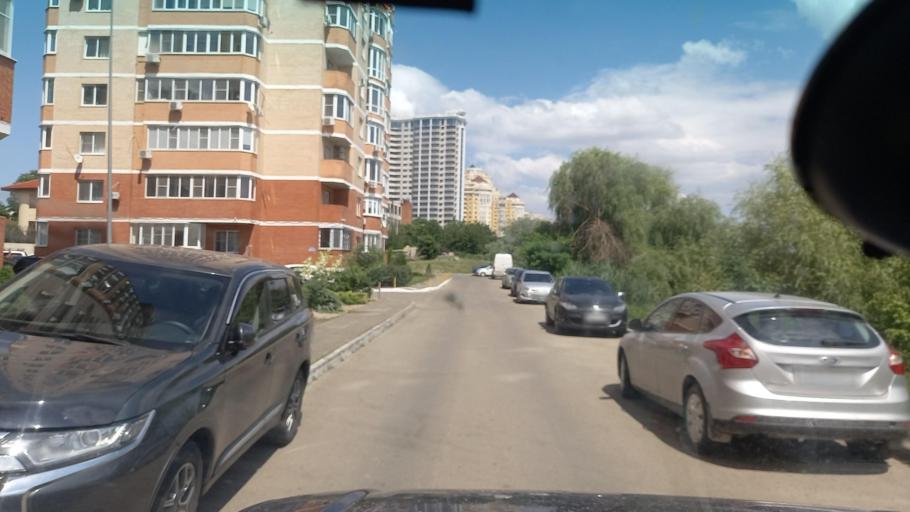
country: RU
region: Krasnodarskiy
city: Krasnodar
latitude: 45.0367
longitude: 38.9363
